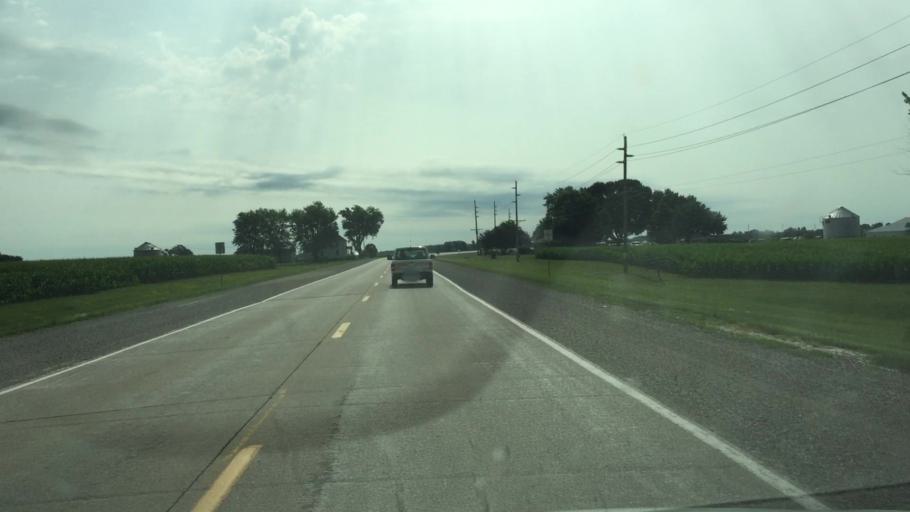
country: US
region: Illinois
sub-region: Hancock County
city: Nauvoo
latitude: 40.6391
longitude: -91.5284
